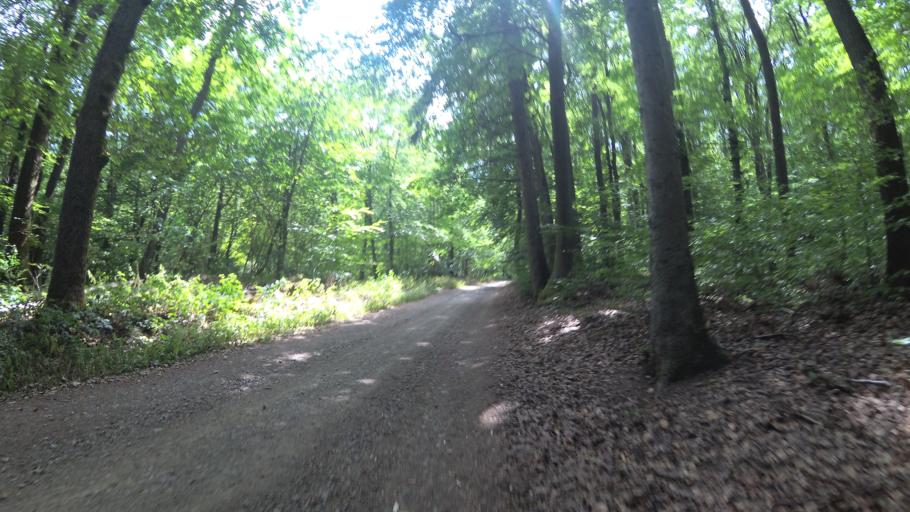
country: DE
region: Rheinland-Pfalz
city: Breitenbach
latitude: 49.4329
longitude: 7.2583
